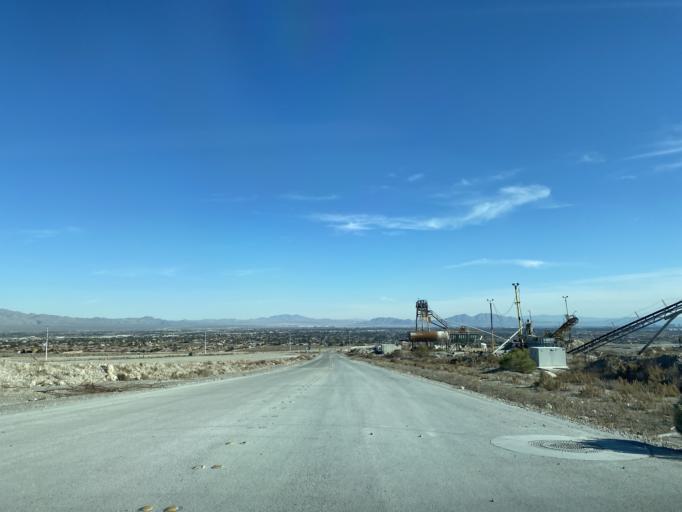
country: US
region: Nevada
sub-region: Clark County
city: Summerlin South
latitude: 36.2552
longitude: -115.3240
